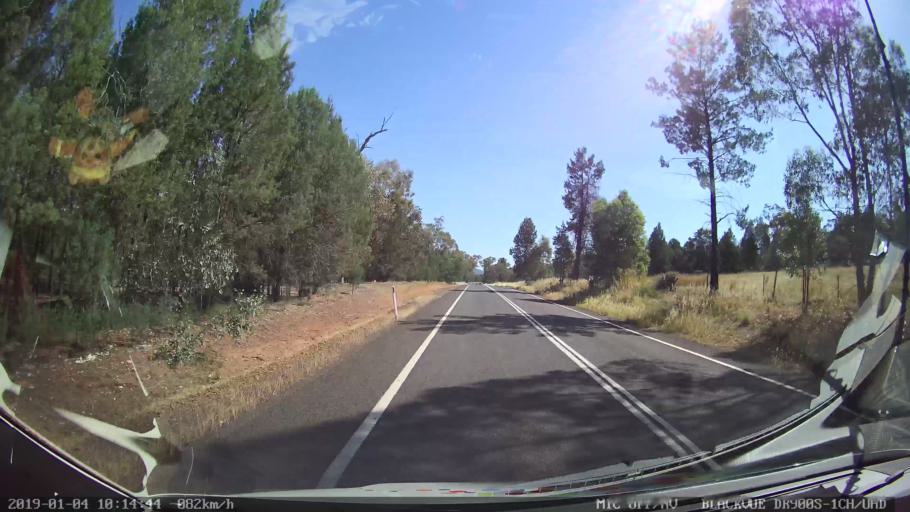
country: AU
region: New South Wales
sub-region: Cabonne
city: Canowindra
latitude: -33.3937
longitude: 148.4155
